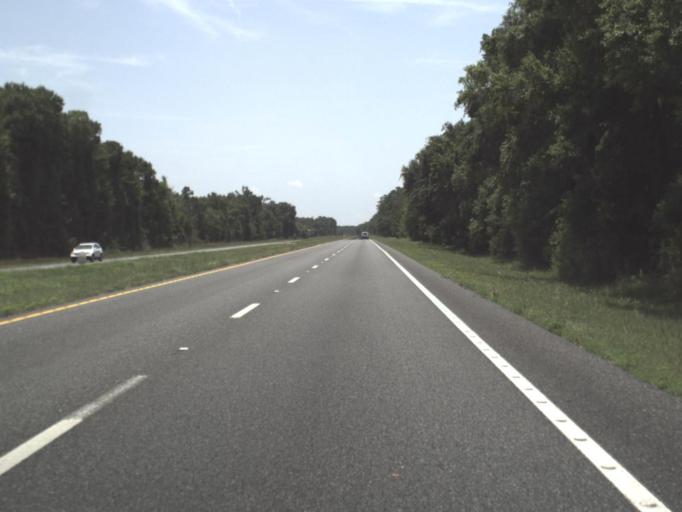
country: US
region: Florida
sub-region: Taylor County
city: Steinhatchee
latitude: 29.8932
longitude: -83.4176
